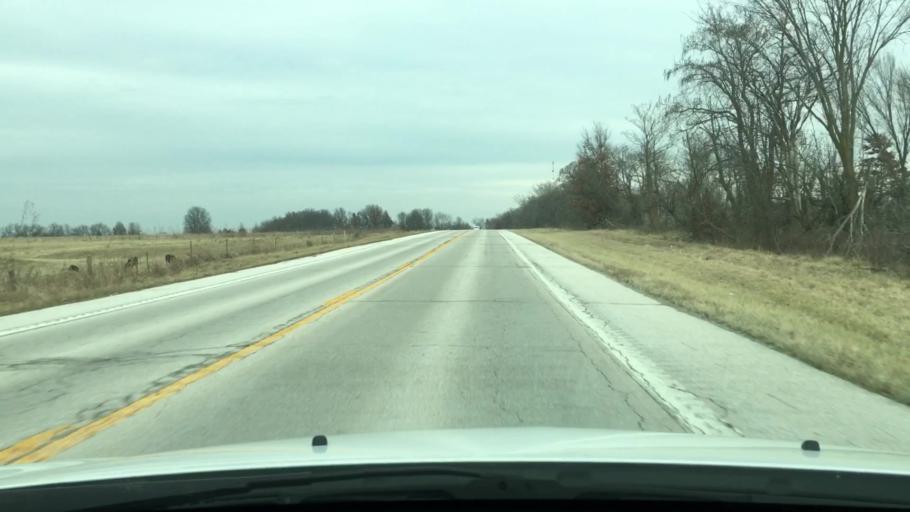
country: US
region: Missouri
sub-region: Audrain County
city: Vandalia
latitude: 39.3346
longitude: -91.4287
